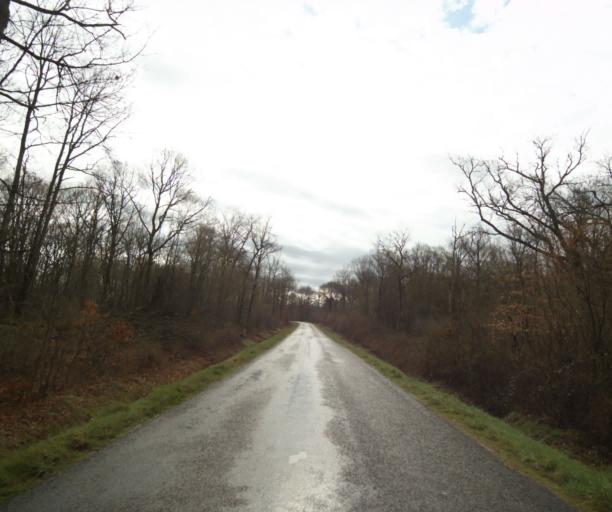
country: FR
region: Auvergne
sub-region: Departement de l'Allier
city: Neuilly-le-Real
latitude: 46.5185
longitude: 3.4267
